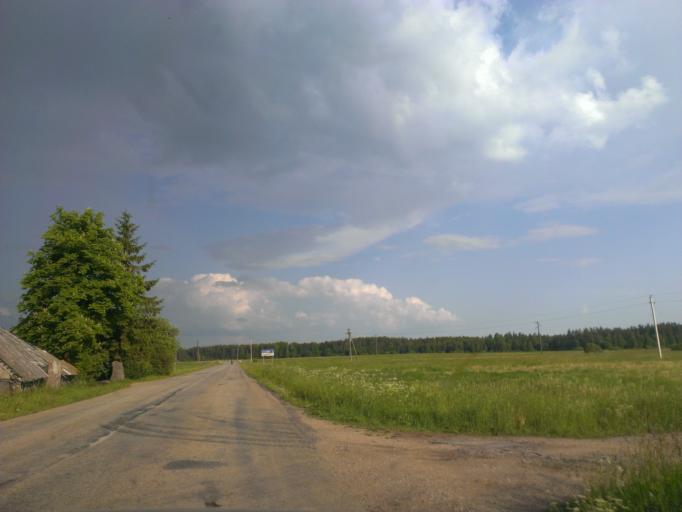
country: LT
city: Salantai
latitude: 56.0684
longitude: 21.4180
